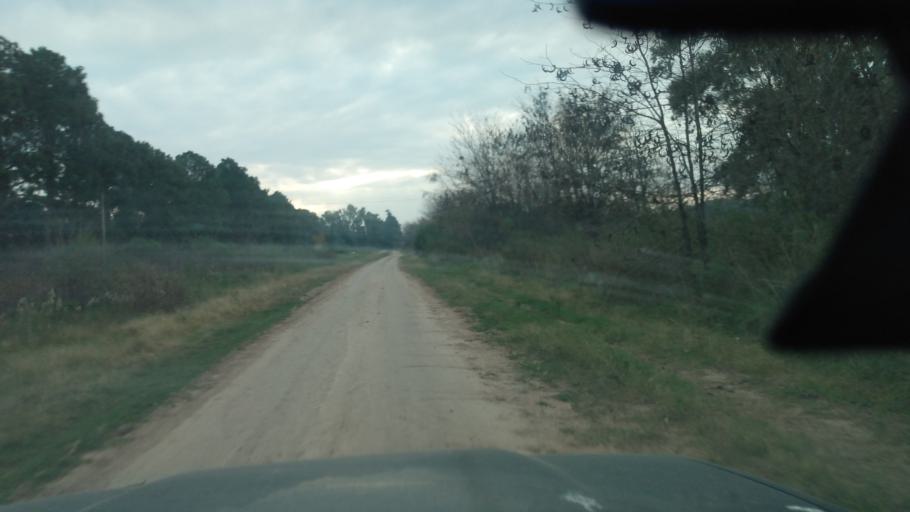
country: AR
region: Buenos Aires
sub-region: Partido de Lujan
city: Lujan
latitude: -34.5620
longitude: -59.1546
